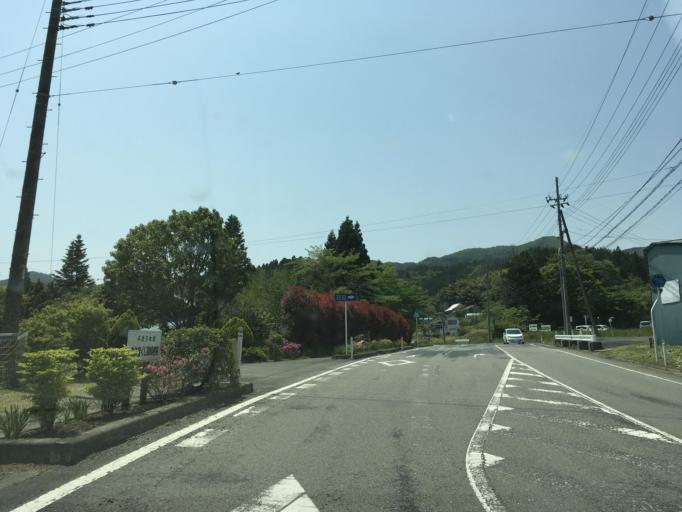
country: JP
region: Iwate
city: Ofunato
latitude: 38.8592
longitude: 141.5232
